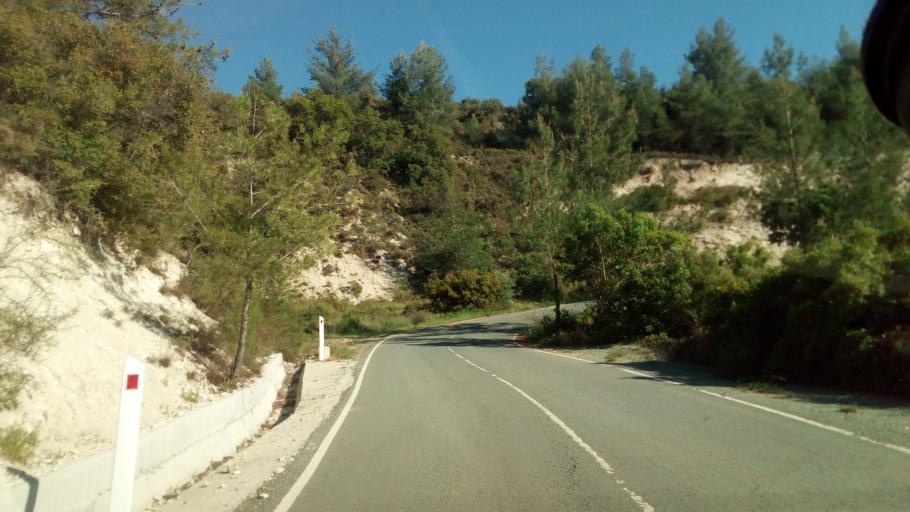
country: CY
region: Limassol
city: Pachna
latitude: 34.8779
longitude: 32.7506
